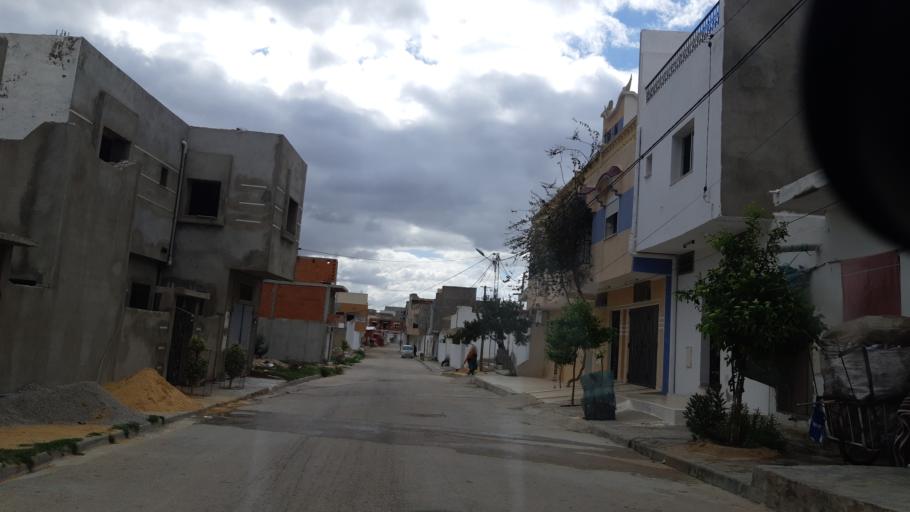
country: TN
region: Susah
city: Akouda
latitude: 35.8715
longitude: 10.5208
